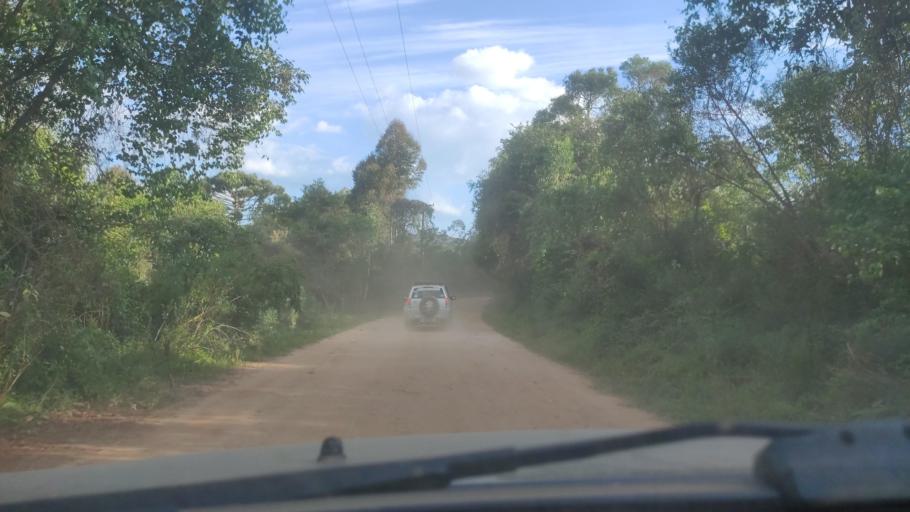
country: BR
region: Minas Gerais
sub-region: Camanducaia
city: Camanducaia
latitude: -22.7673
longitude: -45.9687
